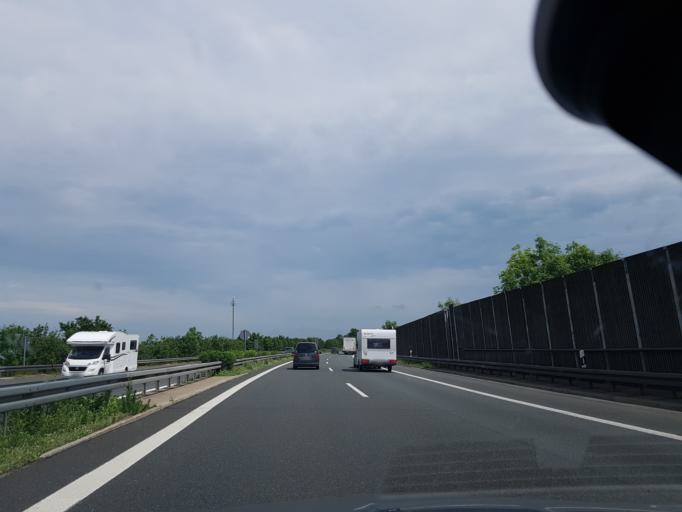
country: DE
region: Saxony
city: Waldkirchen
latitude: 50.6079
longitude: 12.3794
